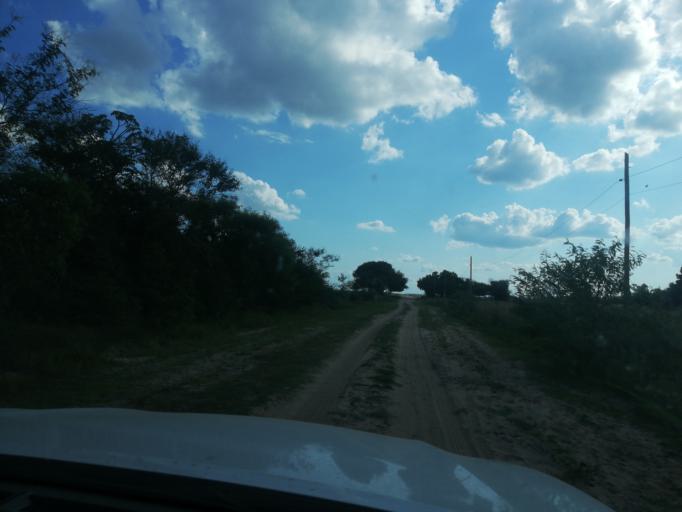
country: AR
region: Corrientes
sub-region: Departamento de San Miguel
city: San Miguel
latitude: -27.9910
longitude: -57.5699
